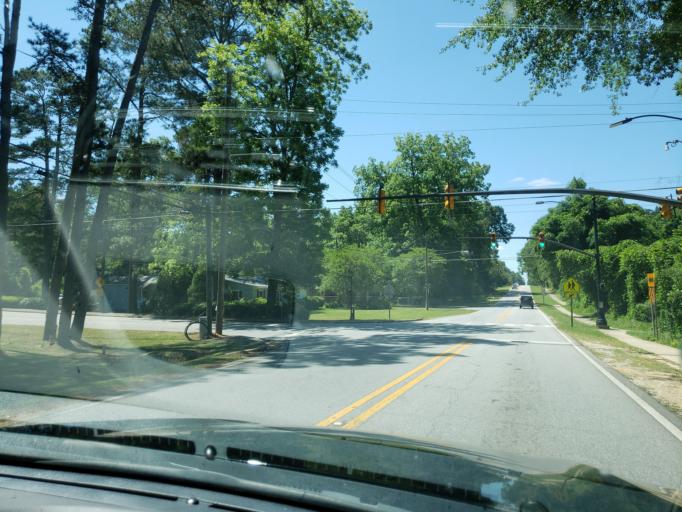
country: US
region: Alabama
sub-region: Lee County
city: Auburn
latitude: 32.6233
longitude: -85.4819
